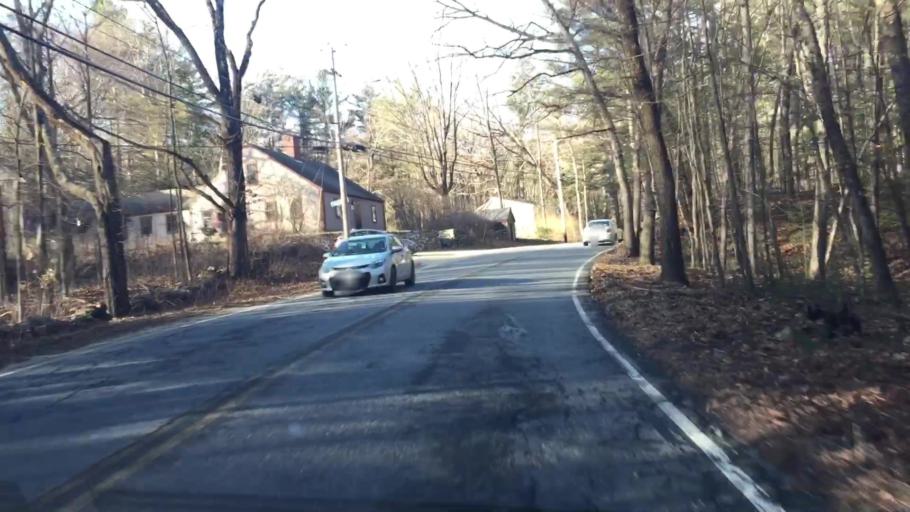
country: US
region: Massachusetts
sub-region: Worcester County
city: Princeton
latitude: 42.4454
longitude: -71.8495
